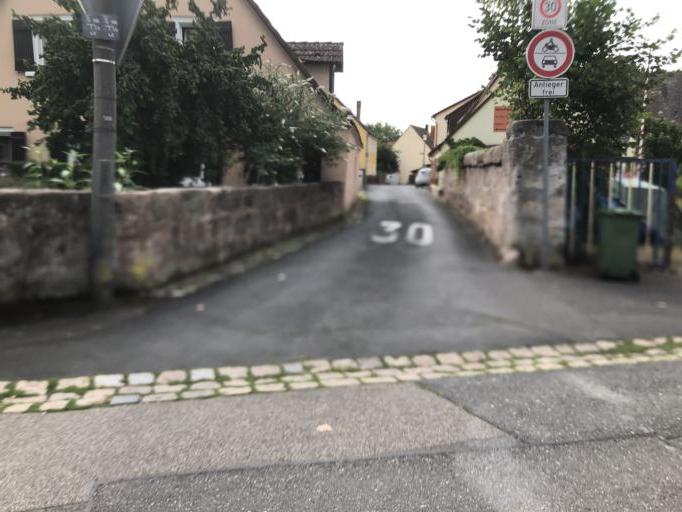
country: DE
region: Bavaria
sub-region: Regierungsbezirk Mittelfranken
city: Erlangen
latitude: 49.5493
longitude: 11.0302
